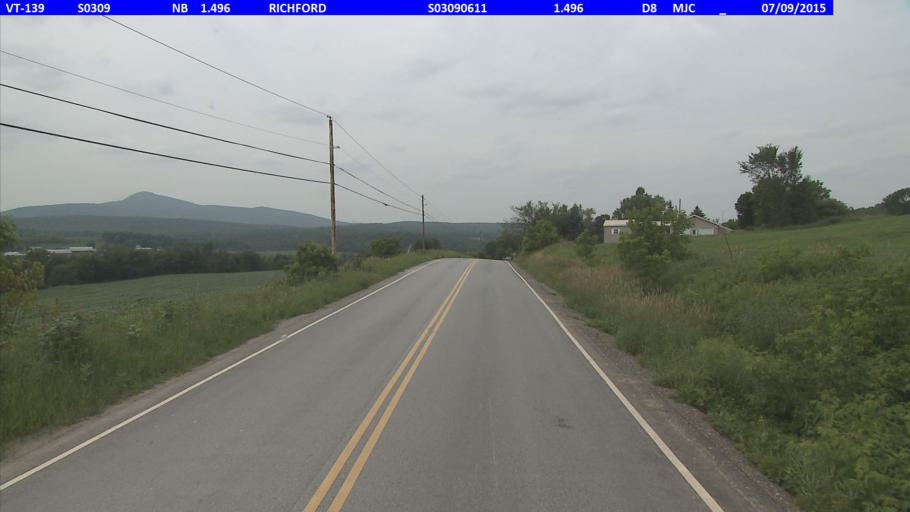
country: US
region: Vermont
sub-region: Franklin County
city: Richford
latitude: 45.0096
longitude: -72.6607
